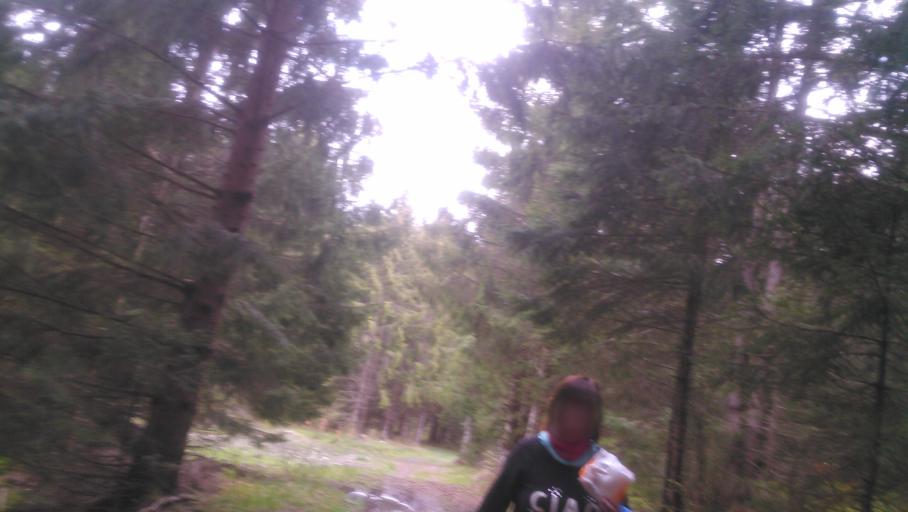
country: SK
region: Banskobystricky
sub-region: Okres Banska Bystrica
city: Brezno
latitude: 48.8745
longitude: 19.5741
